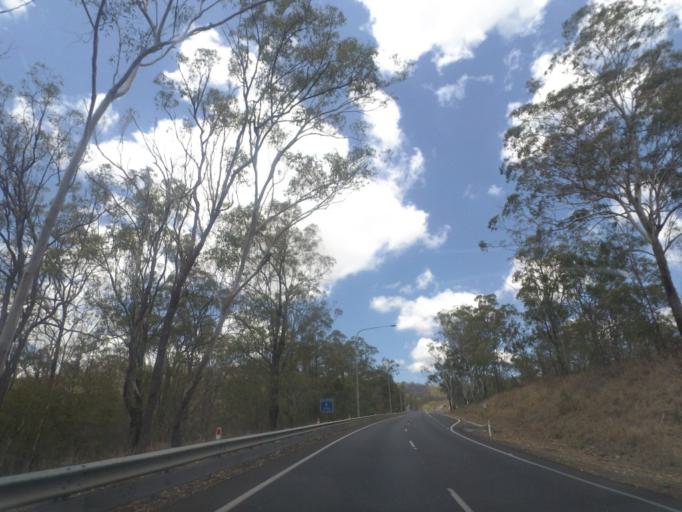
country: AU
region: Queensland
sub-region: Toowoomba
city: East Toowoomba
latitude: -27.5671
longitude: 151.9976
